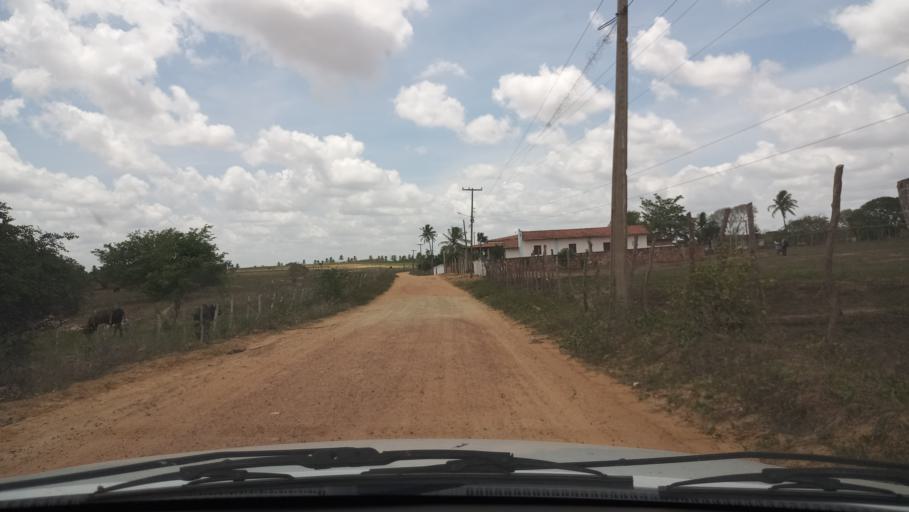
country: BR
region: Rio Grande do Norte
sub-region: Brejinho
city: Brejinho
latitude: -6.3016
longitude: -35.3456
